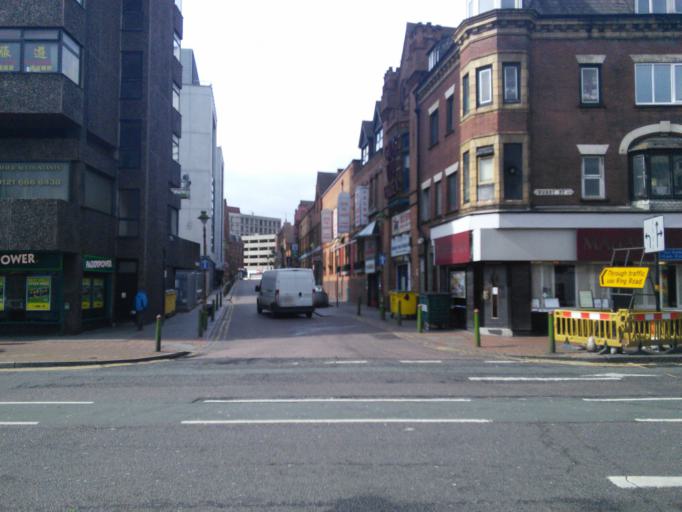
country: GB
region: England
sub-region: City and Borough of Birmingham
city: Birmingham
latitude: 52.4750
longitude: -1.8979
